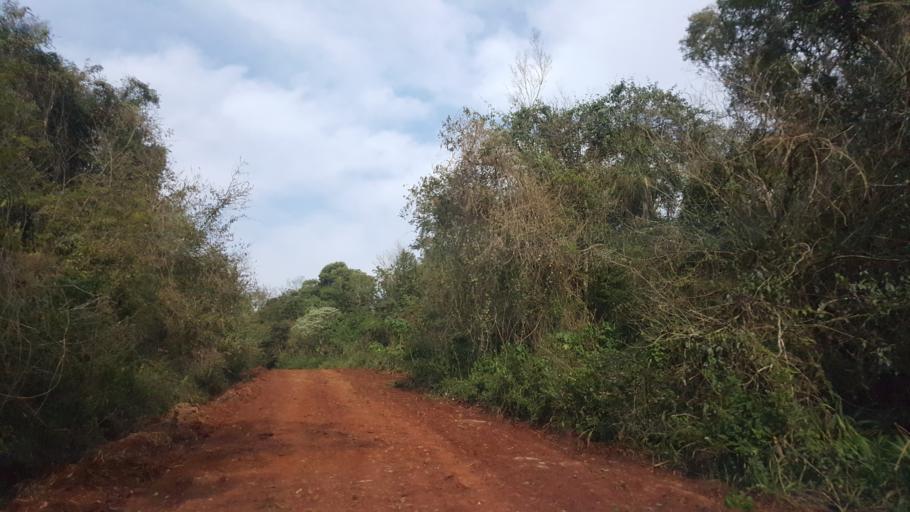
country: AR
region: Misiones
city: Capiovi
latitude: -26.9041
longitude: -55.1148
